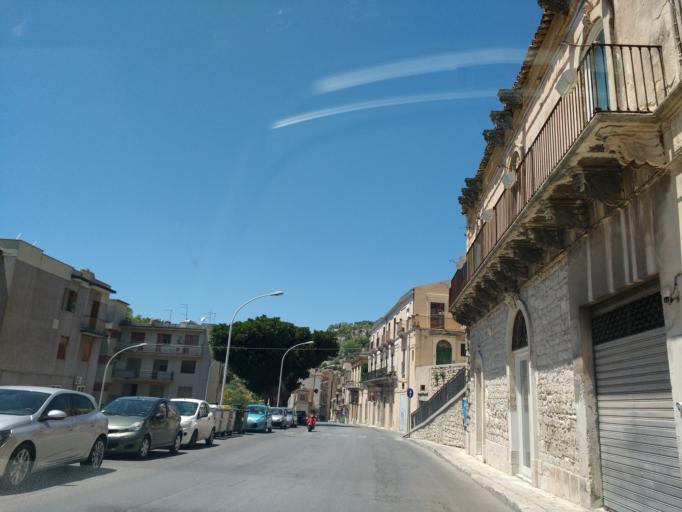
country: IT
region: Sicily
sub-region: Ragusa
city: Modica
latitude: 36.8653
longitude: 14.7592
